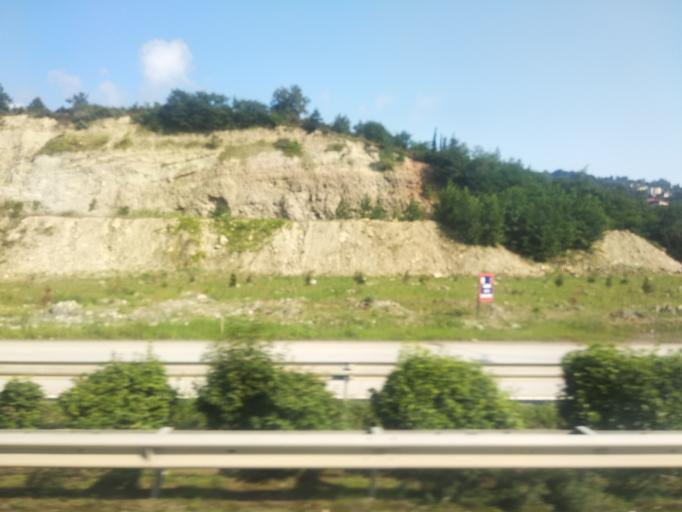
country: TR
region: Ordu
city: Ordu
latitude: 41.0003
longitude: 37.8228
